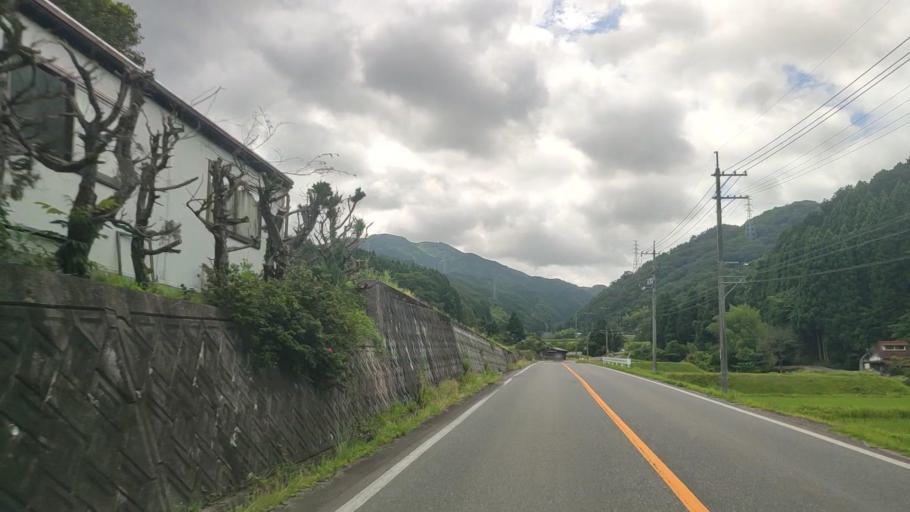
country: JP
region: Tottori
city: Yonago
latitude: 35.2909
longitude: 133.4215
